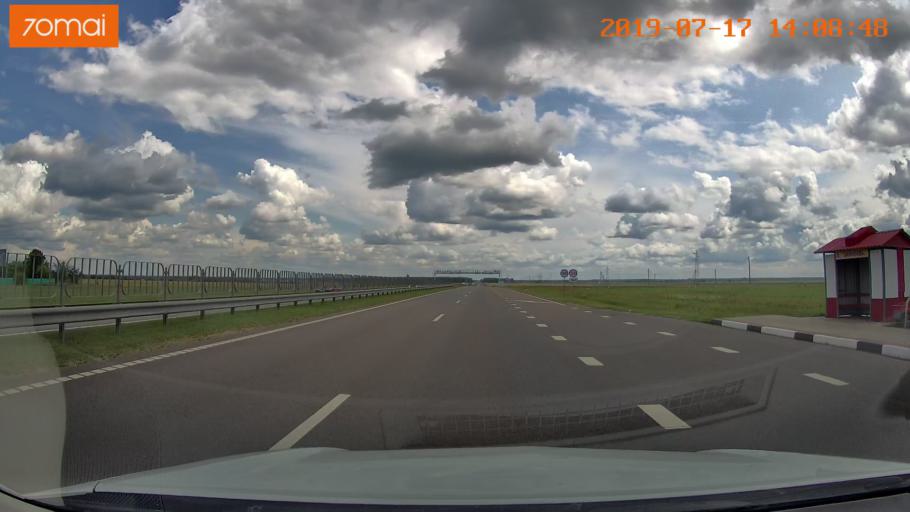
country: BY
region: Mogilev
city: Yalizava
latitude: 53.2341
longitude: 28.9774
